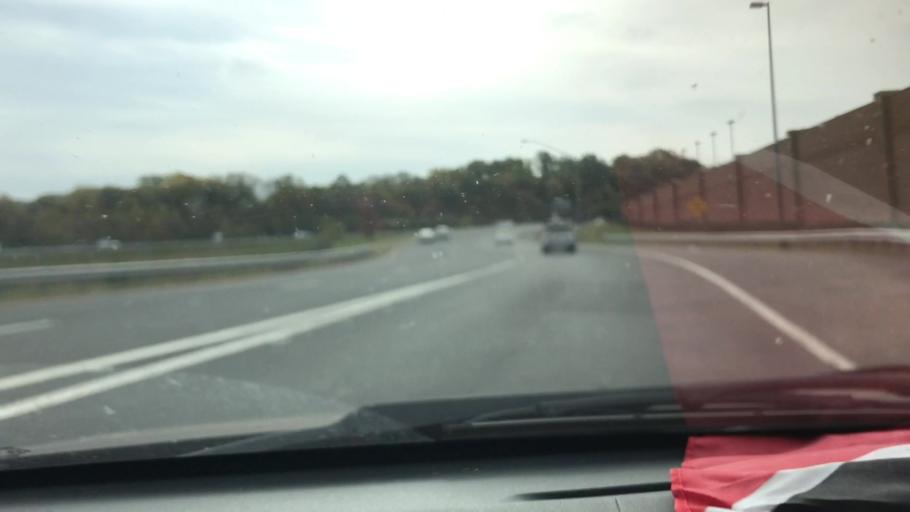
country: US
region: Maryland
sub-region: Prince George's County
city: Largo
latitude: 38.8683
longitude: -76.8475
